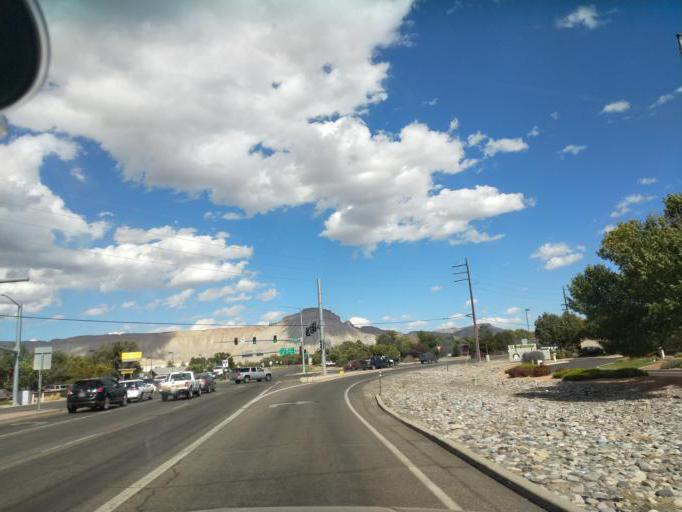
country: US
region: Colorado
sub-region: Mesa County
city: Clifton
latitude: 39.0913
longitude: -108.4538
